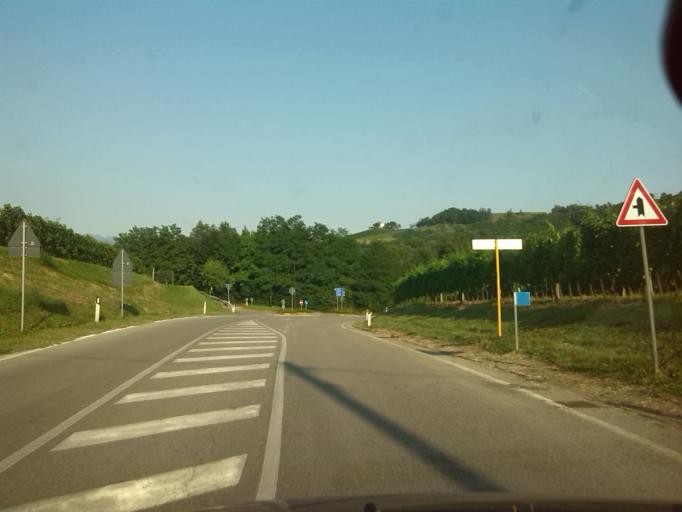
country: IT
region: Friuli Venezia Giulia
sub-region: Provincia di Udine
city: Corno di Rosazzo
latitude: 46.0037
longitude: 13.4671
